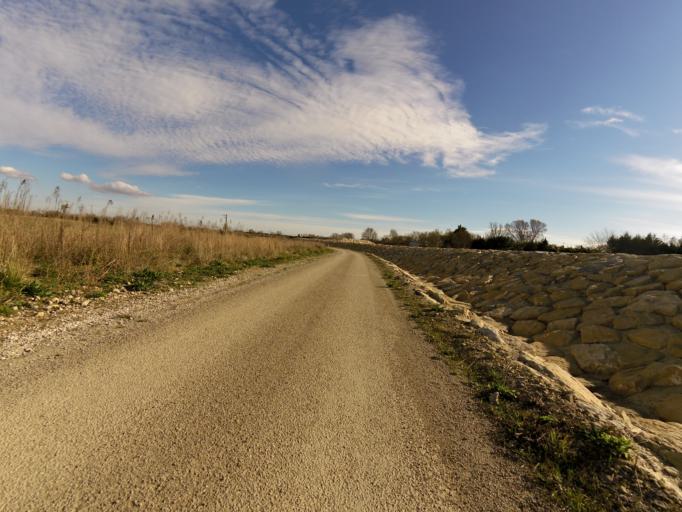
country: FR
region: Languedoc-Roussillon
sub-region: Departement du Gard
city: Gallargues-le-Montueux
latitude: 43.7148
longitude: 4.1565
